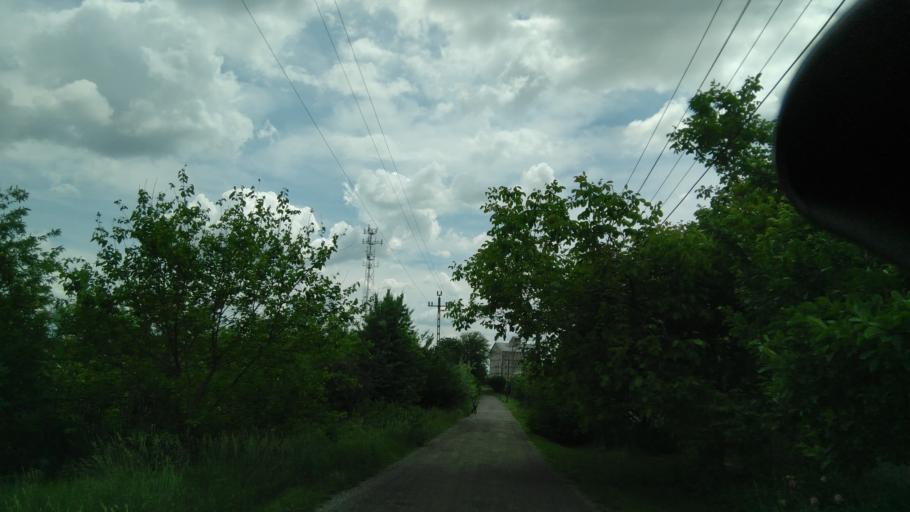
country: HU
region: Bekes
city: Totkomlos
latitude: 46.4146
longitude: 20.7261
